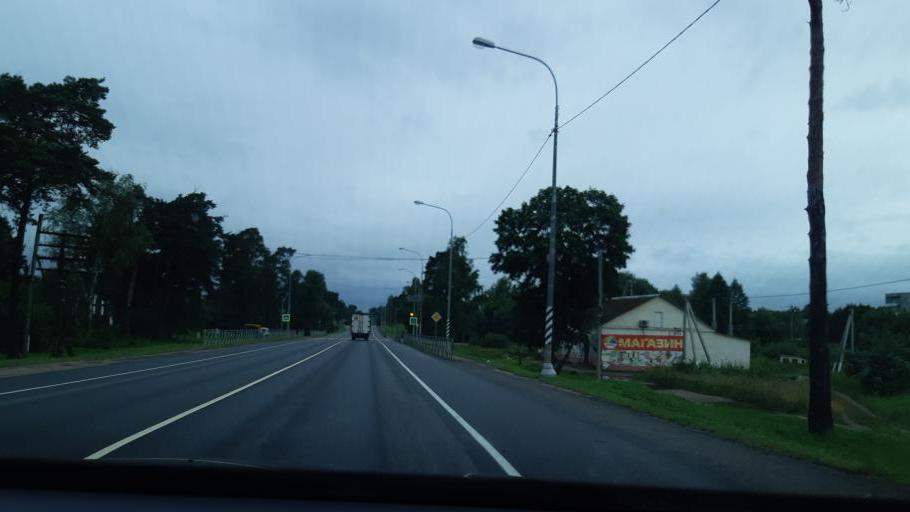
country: RU
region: Smolensk
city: Oster
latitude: 53.9912
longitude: 32.8188
